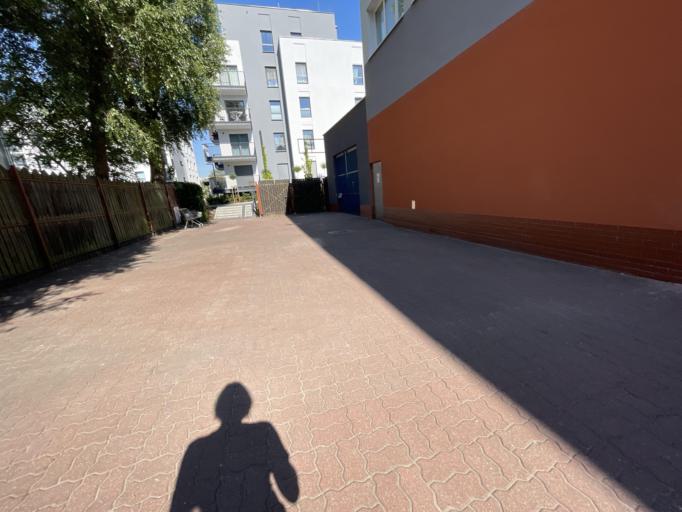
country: PL
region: Kujawsko-Pomorskie
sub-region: Bydgoszcz
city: Bydgoszcz
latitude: 53.1336
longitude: 18.0181
